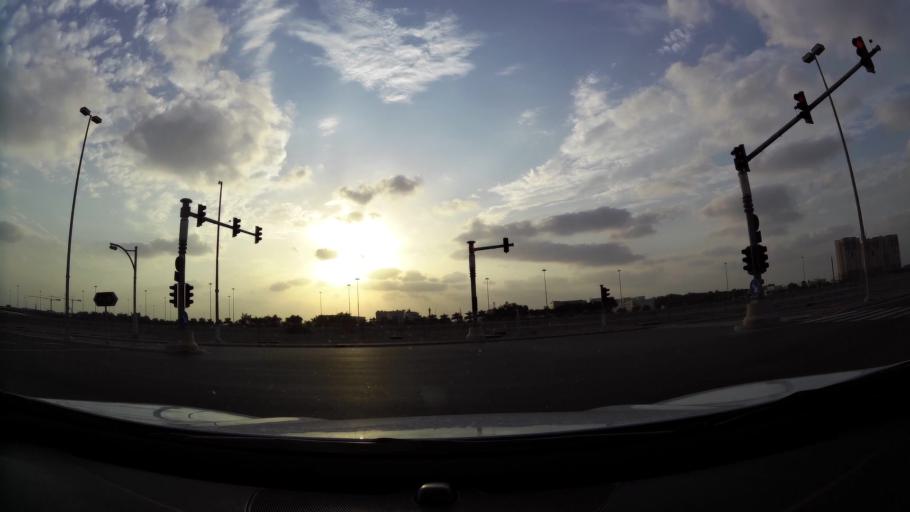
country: AE
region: Abu Dhabi
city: Abu Dhabi
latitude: 24.3784
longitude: 54.5276
